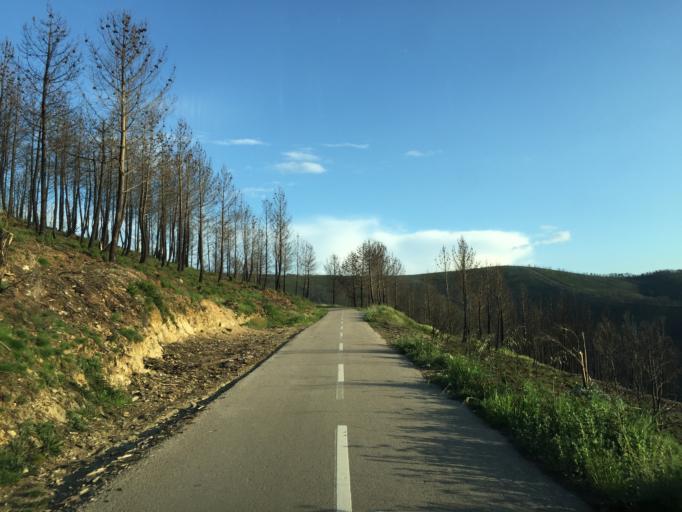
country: PT
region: Coimbra
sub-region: Gois
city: Gois
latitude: 40.1260
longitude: -8.0175
